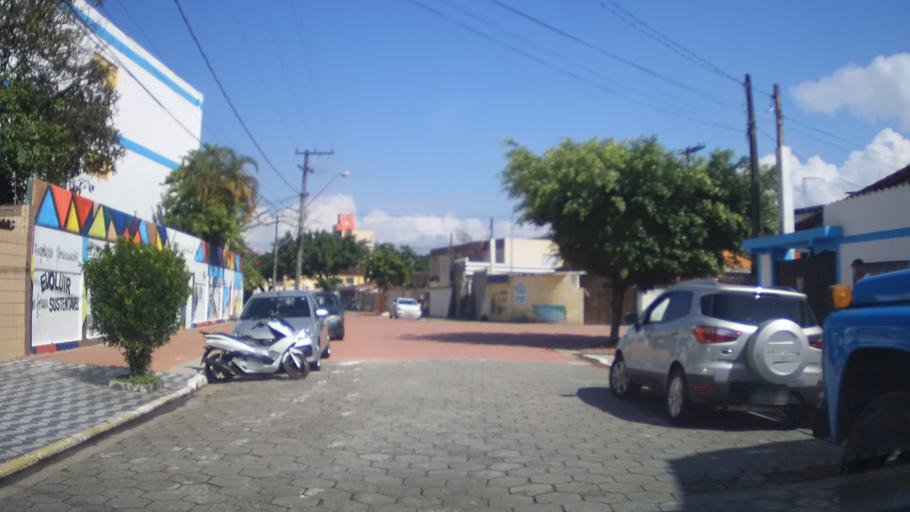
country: BR
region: Sao Paulo
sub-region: Praia Grande
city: Praia Grande
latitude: -24.0062
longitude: -46.4220
